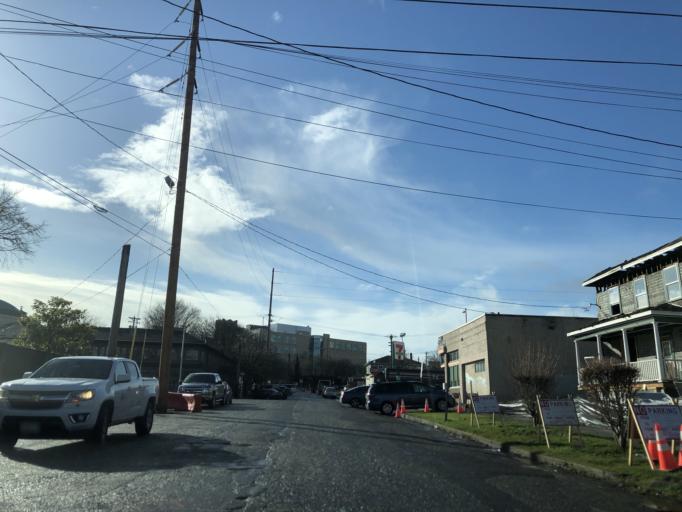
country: US
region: Washington
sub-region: Pierce County
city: Tacoma
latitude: 47.2629
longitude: -122.4513
